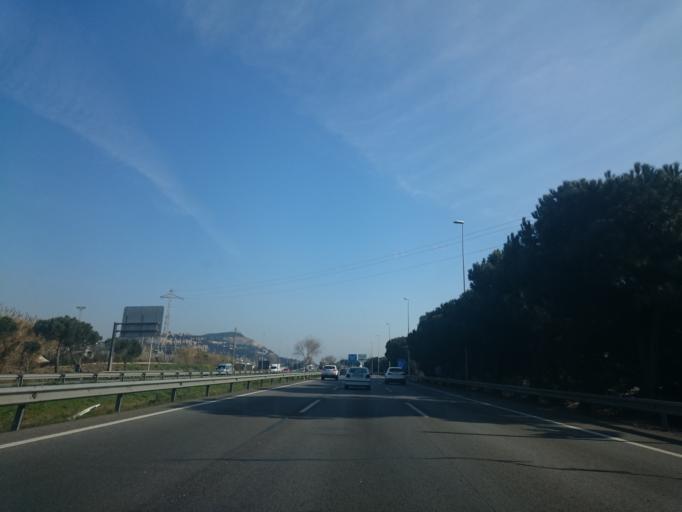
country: ES
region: Catalonia
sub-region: Provincia de Barcelona
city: Sants-Montjuic
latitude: 41.3456
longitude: 2.1377
